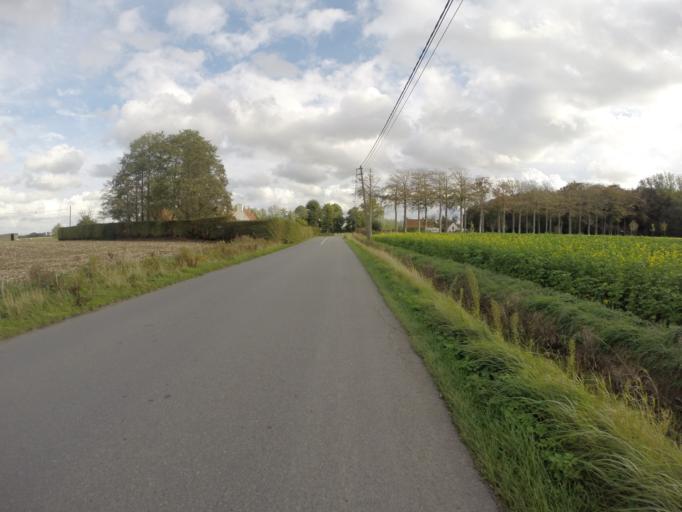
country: BE
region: Flanders
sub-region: Provincie Oost-Vlaanderen
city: Aalter
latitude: 51.0777
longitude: 3.4151
